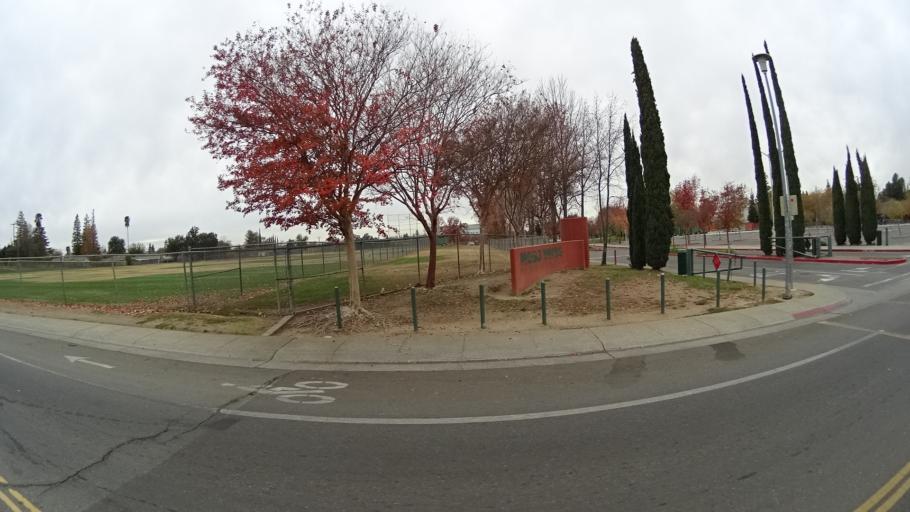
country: US
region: California
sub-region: Sacramento County
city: Citrus Heights
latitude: 38.7011
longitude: -121.2950
